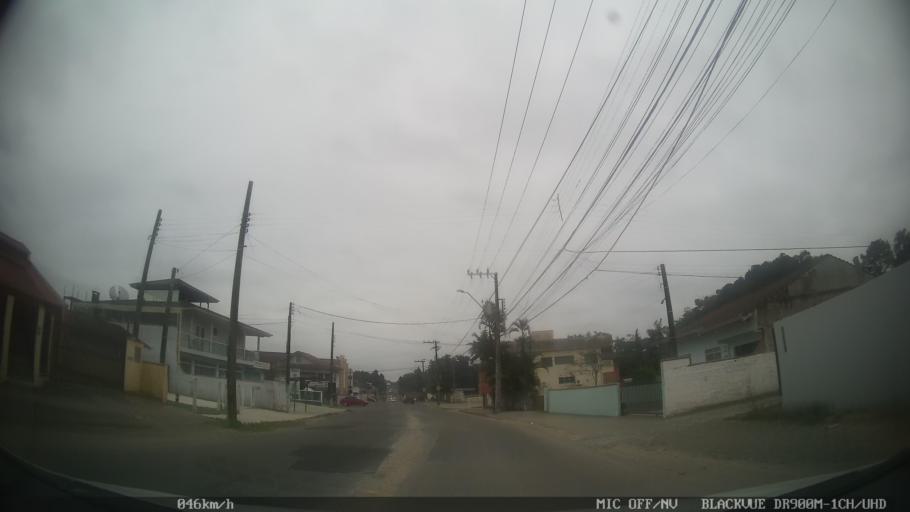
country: BR
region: Santa Catarina
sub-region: Joinville
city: Joinville
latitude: -26.3593
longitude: -48.8457
